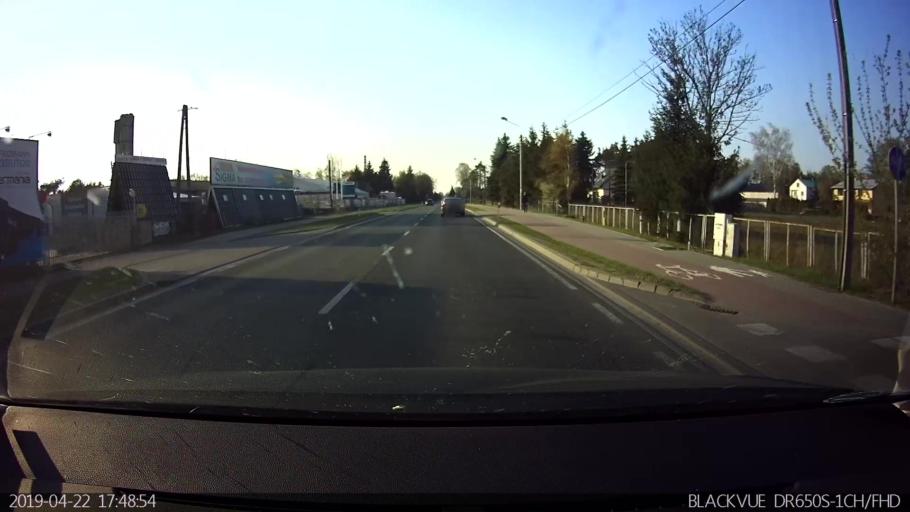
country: PL
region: Masovian Voivodeship
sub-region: Powiat wegrowski
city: Wegrow
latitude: 52.4091
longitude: 22.0119
